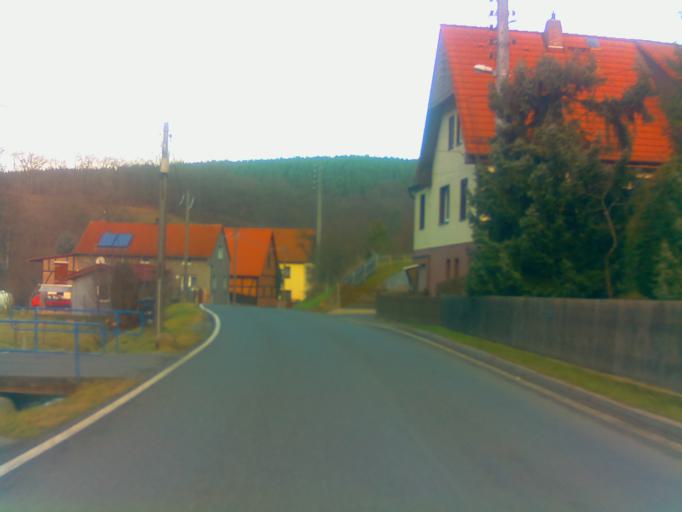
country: DE
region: Thuringia
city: Unterwellenborn
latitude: 50.6947
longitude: 11.3984
